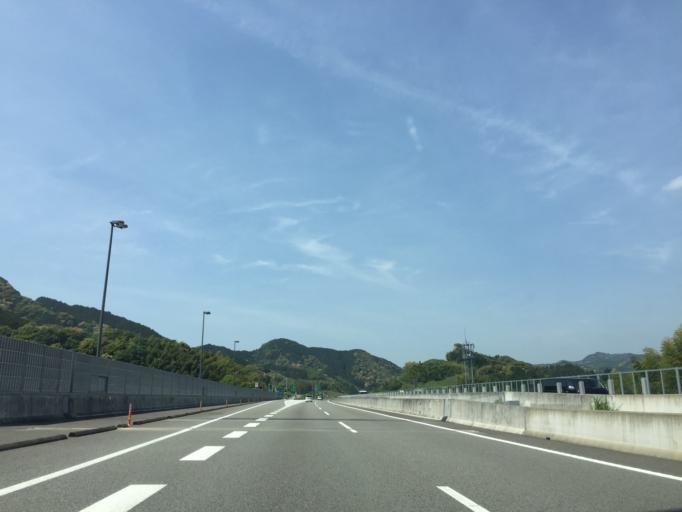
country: JP
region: Shizuoka
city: Fujieda
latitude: 34.8963
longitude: 138.2385
